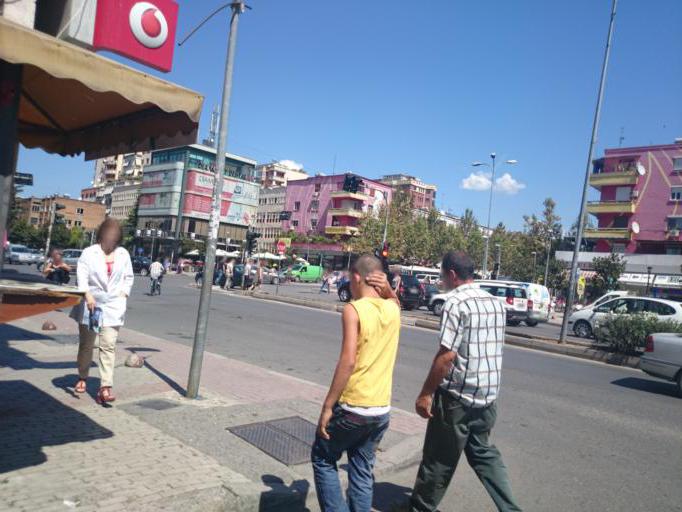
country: AL
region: Tirane
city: Tirana
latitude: 41.3254
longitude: 19.8033
